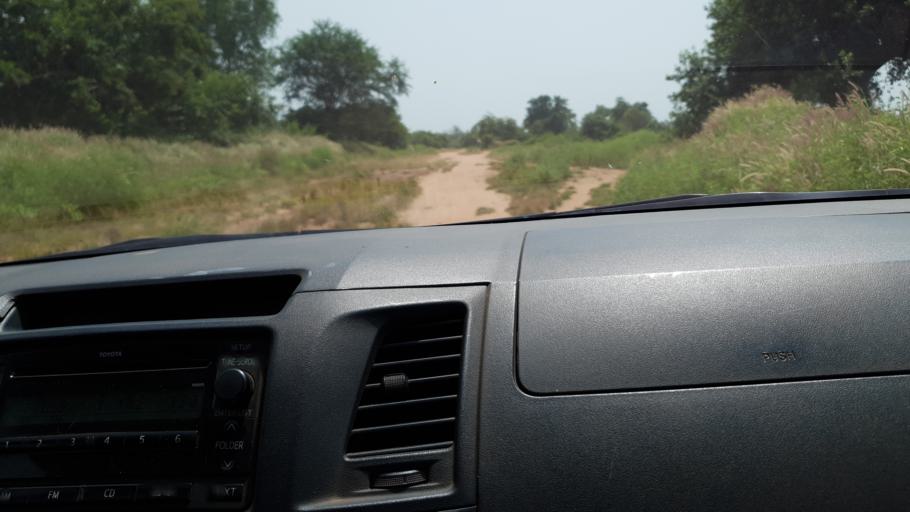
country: ML
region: Koulikoro
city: Kolokani
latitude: 13.4264
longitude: -8.2414
